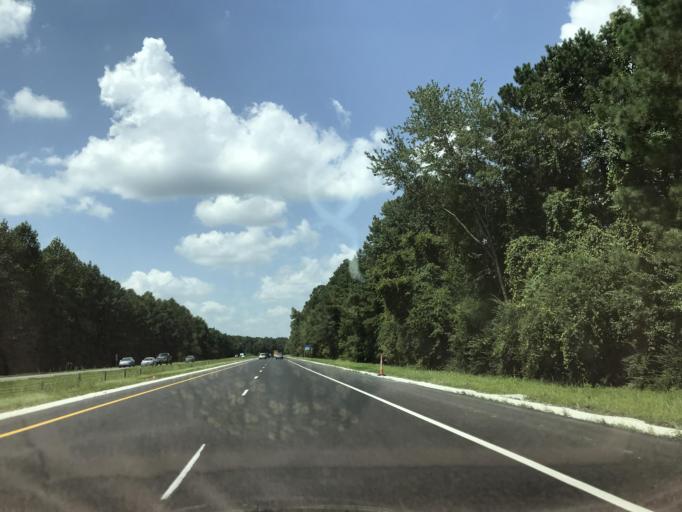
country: US
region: North Carolina
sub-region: Duplin County
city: Warsaw
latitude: 34.9545
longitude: -78.0951
